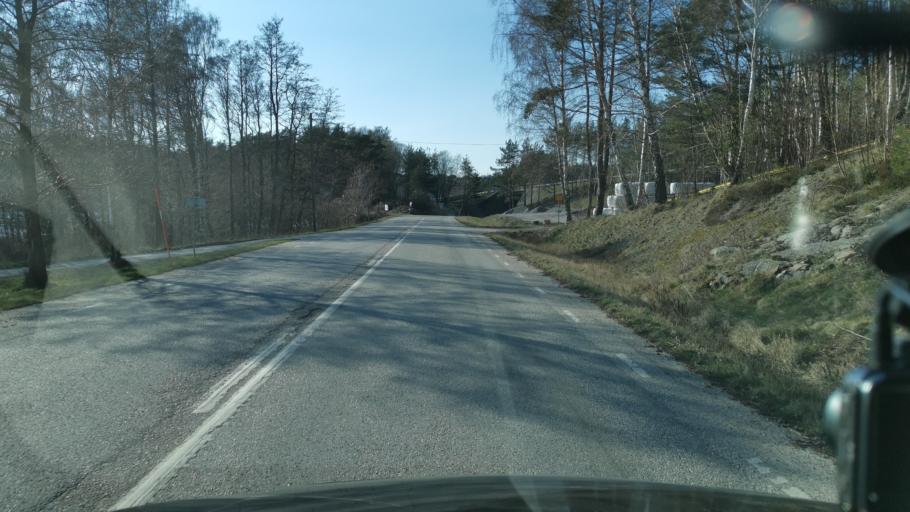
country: SE
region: Vaestra Goetaland
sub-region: Tjorns Kommun
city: Myggenas
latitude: 58.0564
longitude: 11.7685
